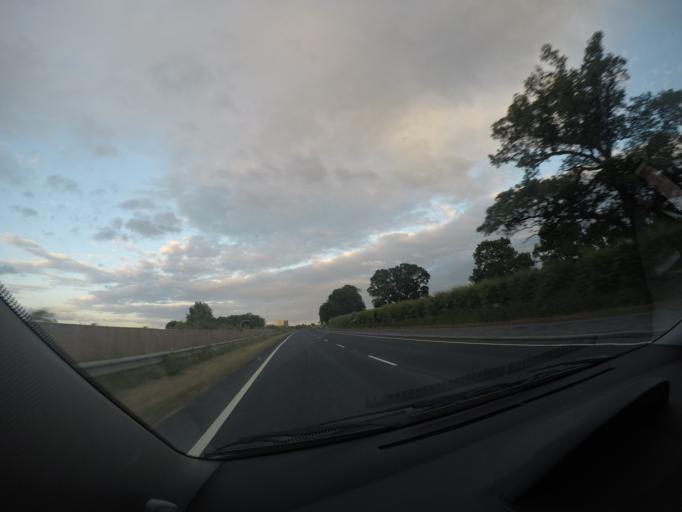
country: GB
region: England
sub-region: North Yorkshire
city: Bedale
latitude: 54.2935
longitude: -1.5529
